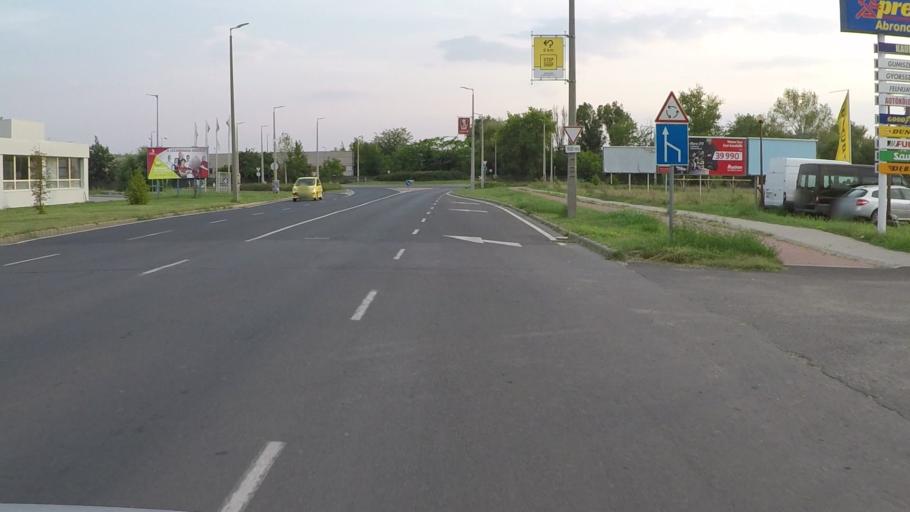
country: HU
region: Jasz-Nagykun-Szolnok
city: Szolnok
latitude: 47.1935
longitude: 20.1734
